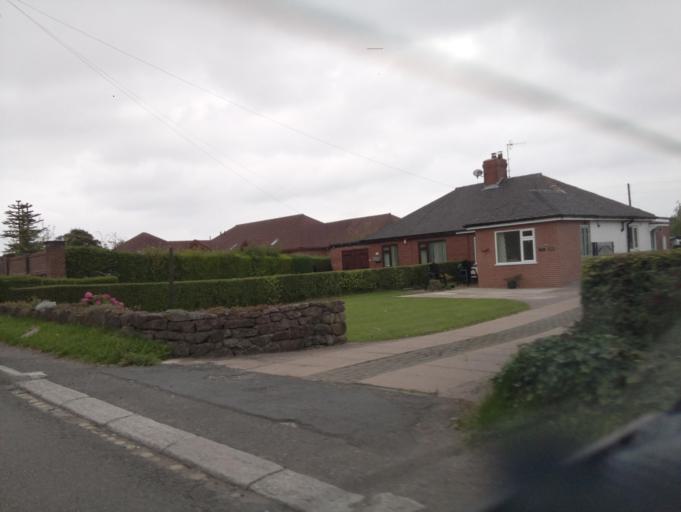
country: GB
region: England
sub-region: Staffordshire
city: Cheddleton
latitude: 53.0261
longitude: -2.0713
